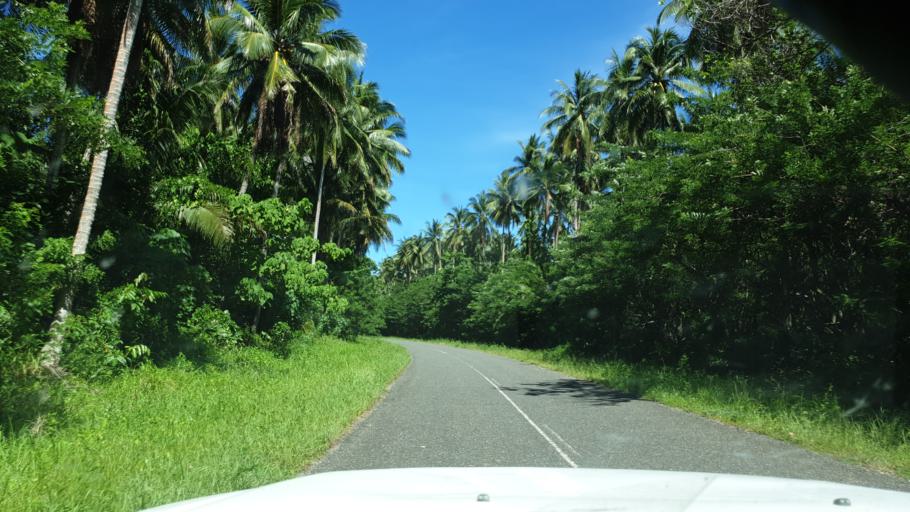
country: PG
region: Madang
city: Madang
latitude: -4.4670
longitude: 145.4151
